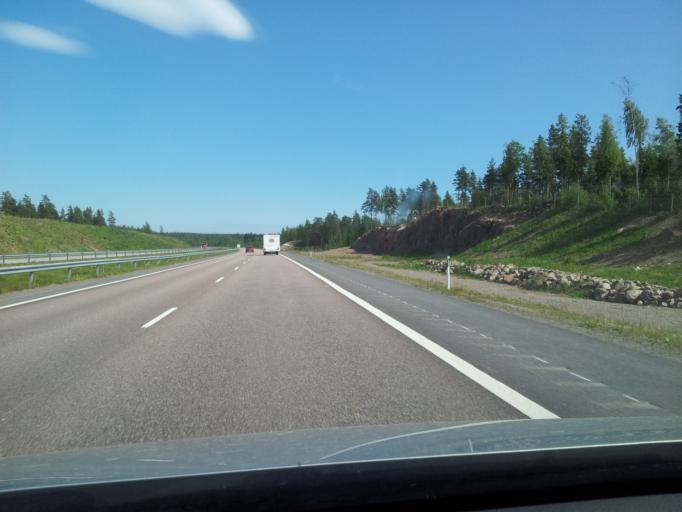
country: FI
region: Uusimaa
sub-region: Loviisa
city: Perna
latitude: 60.4804
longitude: 26.0317
